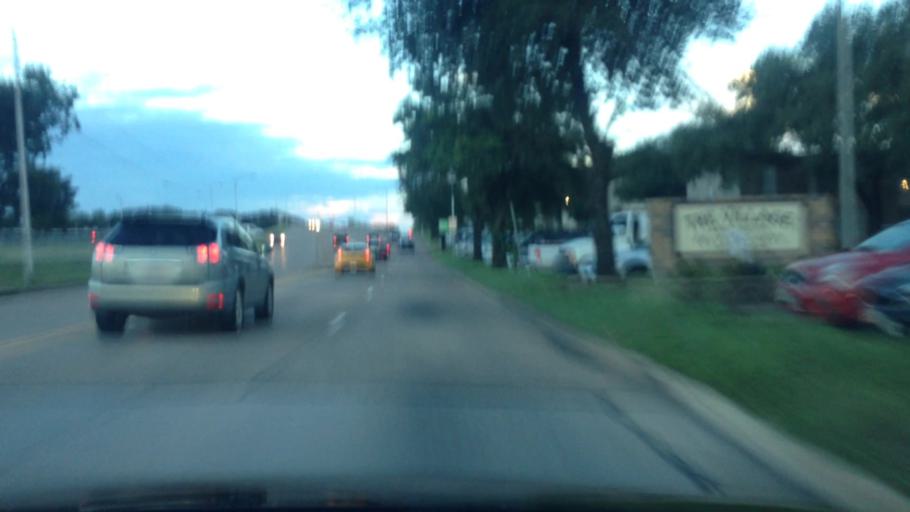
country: US
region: Texas
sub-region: Tarrant County
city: Arlington
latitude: 32.7396
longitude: -97.1319
